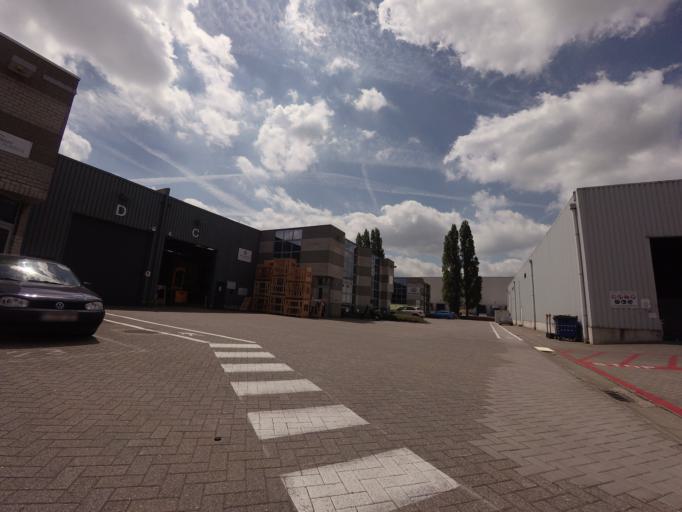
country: BE
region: Flanders
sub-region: Provincie Antwerpen
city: Kontich
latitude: 51.1208
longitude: 4.4615
